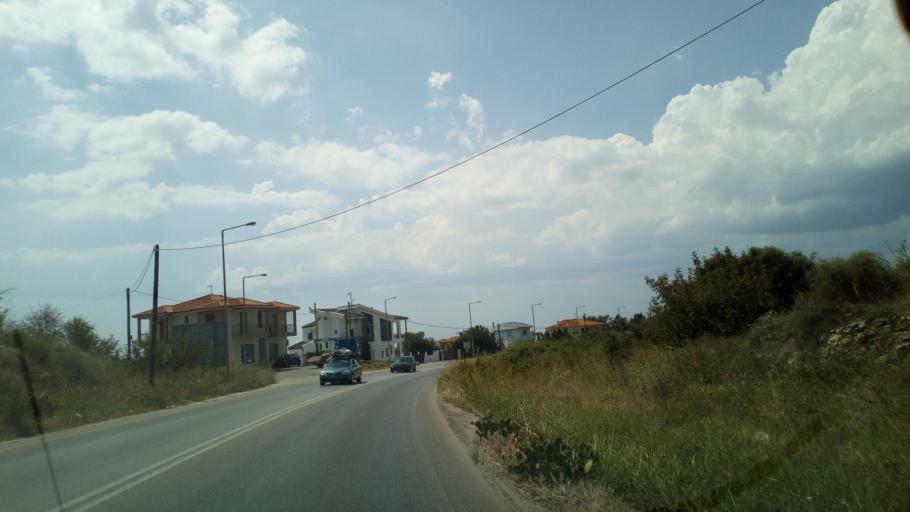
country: GR
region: Central Macedonia
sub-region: Nomos Chalkidikis
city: Nikiti
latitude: 40.2146
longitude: 23.6830
